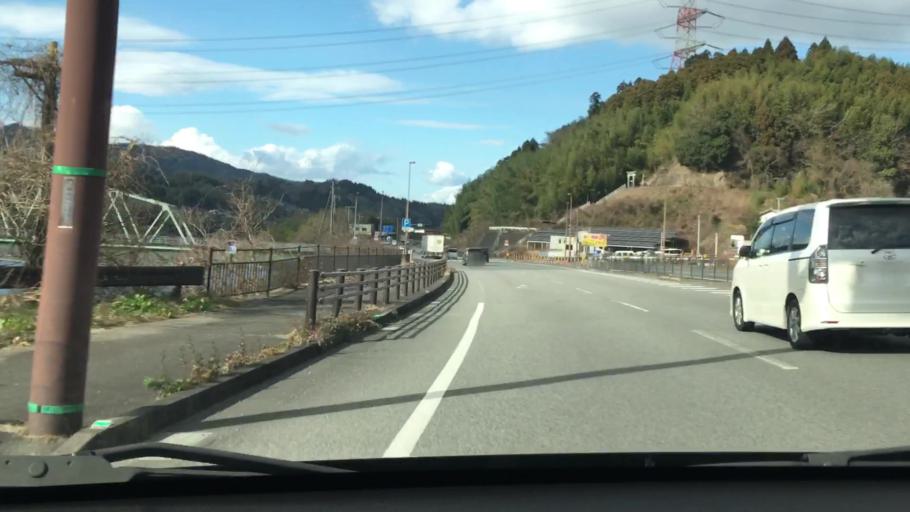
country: JP
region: Oita
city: Oita
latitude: 33.1119
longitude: 131.6565
